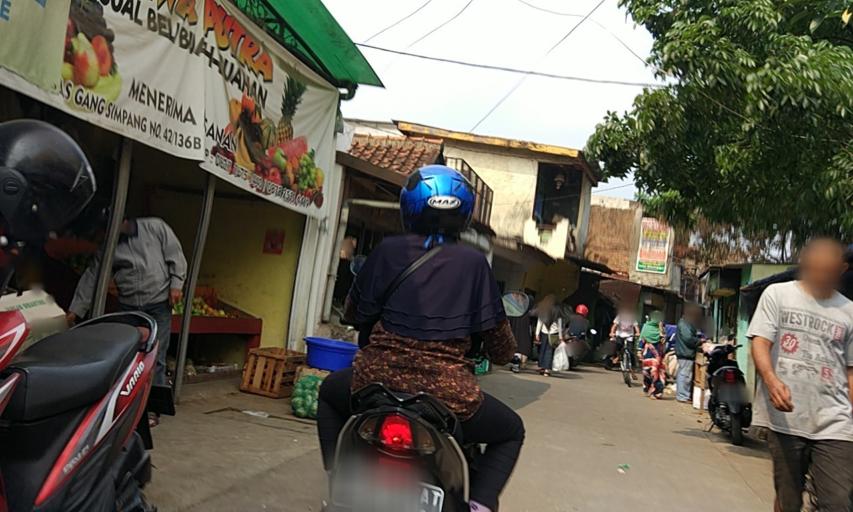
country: ID
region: West Java
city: Bandung
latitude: -6.9111
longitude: 107.6448
